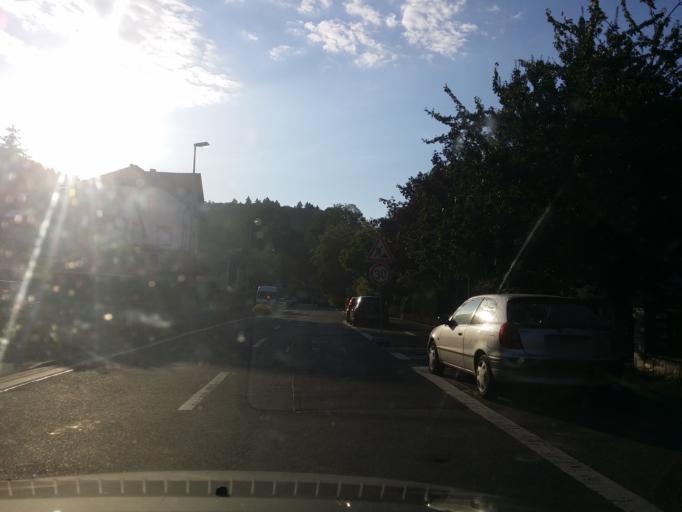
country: DE
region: Hesse
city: Kelkheim (Taunus)
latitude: 50.1186
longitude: 8.4193
